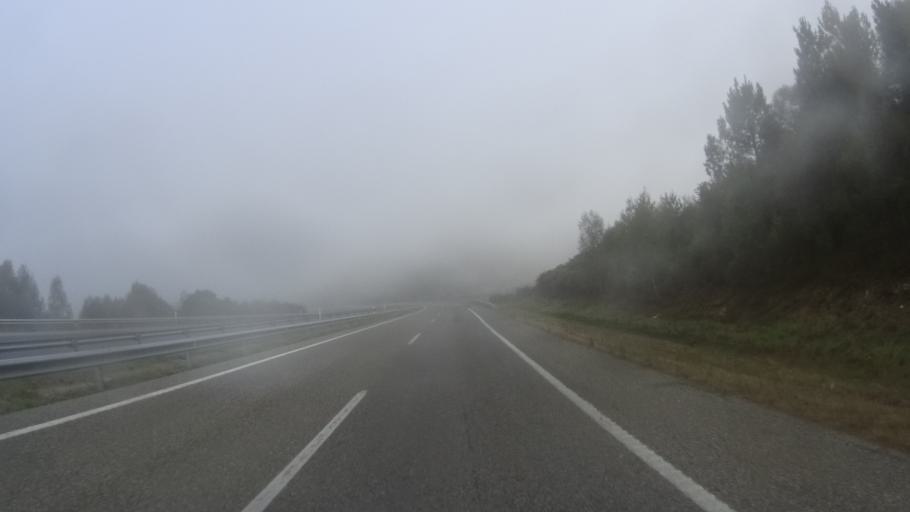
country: ES
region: Galicia
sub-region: Provincia de Lugo
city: Becerrea
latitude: 42.9052
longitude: -7.1909
